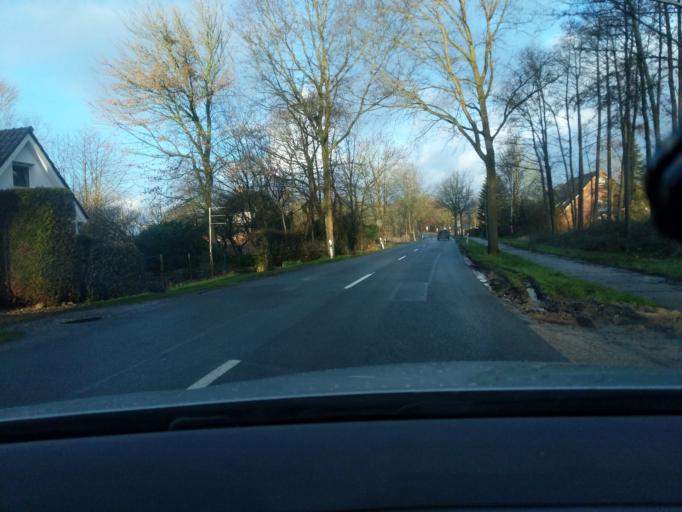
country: DE
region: Lower Saxony
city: Cuxhaven
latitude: 53.8282
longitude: 8.7279
